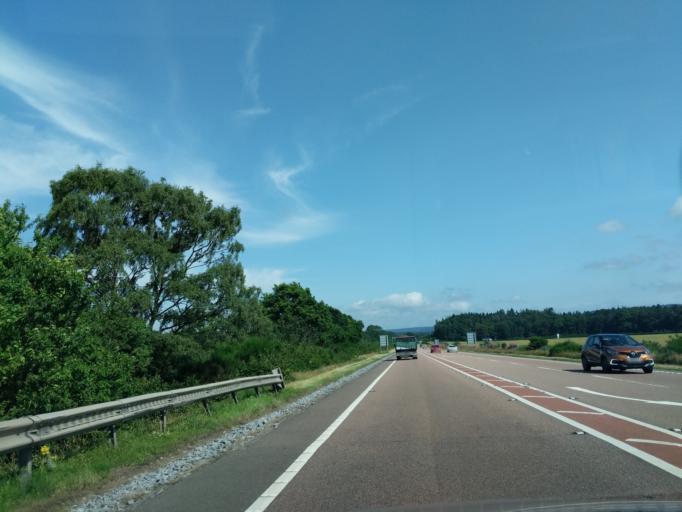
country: GB
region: Scotland
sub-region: Moray
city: Fochabers
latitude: 57.6231
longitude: -3.1265
